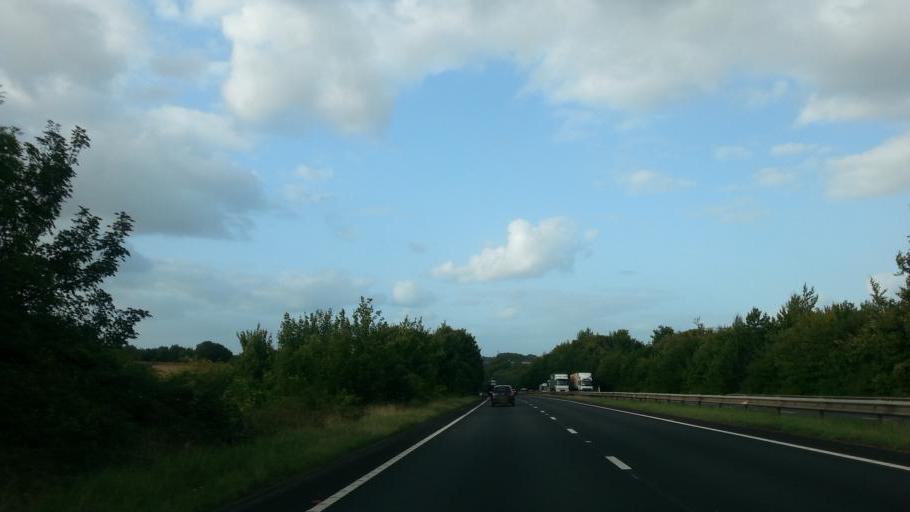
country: GB
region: England
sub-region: Hampshire
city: Kings Worthy
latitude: 51.1648
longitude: -1.3415
